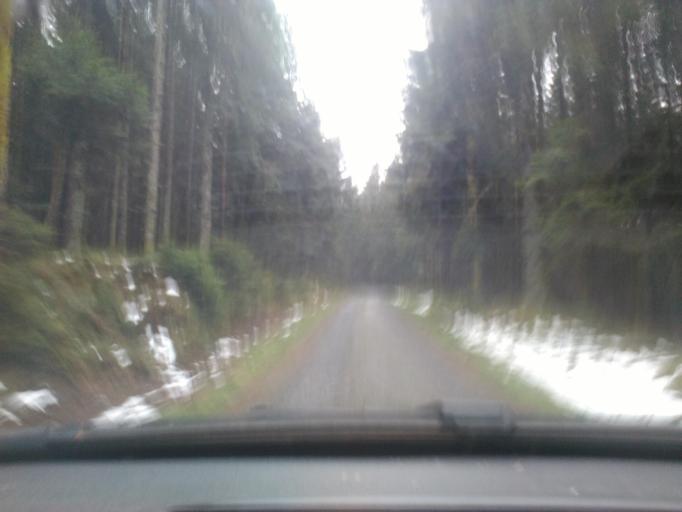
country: FR
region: Lorraine
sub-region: Departement des Vosges
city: Gerardmer
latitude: 48.1169
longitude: 6.8698
